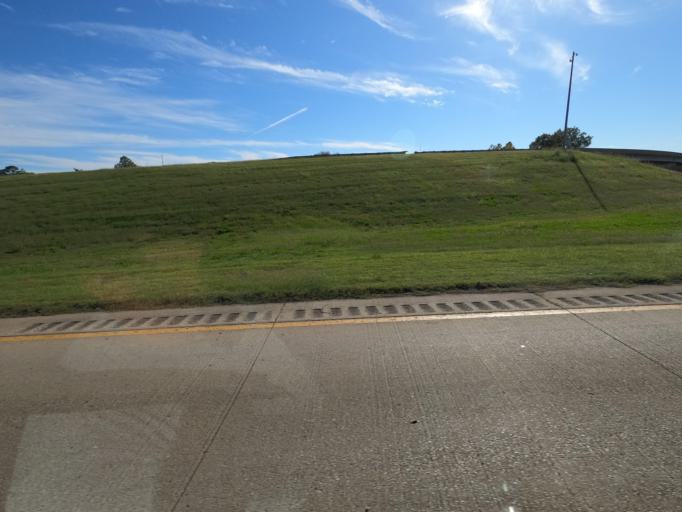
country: US
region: Arkansas
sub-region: Crittenden County
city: West Memphis
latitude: 35.1479
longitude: -90.1303
